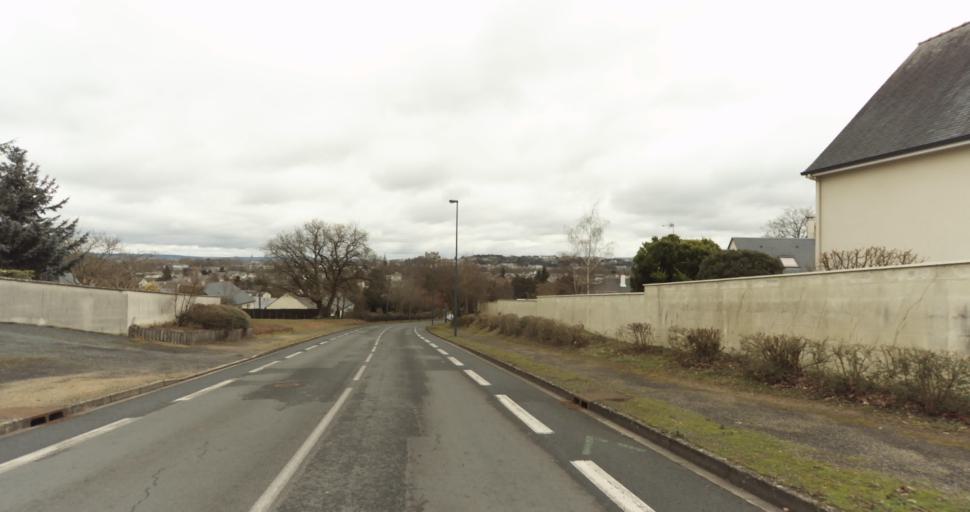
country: FR
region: Pays de la Loire
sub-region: Departement de Maine-et-Loire
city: Saumur
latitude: 47.2510
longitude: -0.0994
